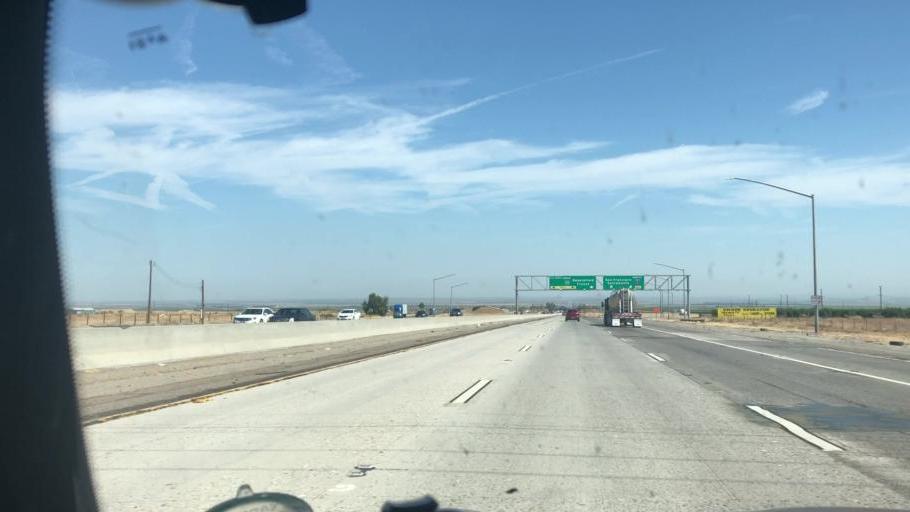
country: US
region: California
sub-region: Kern County
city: Frazier Park
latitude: 35.0054
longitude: -118.9513
